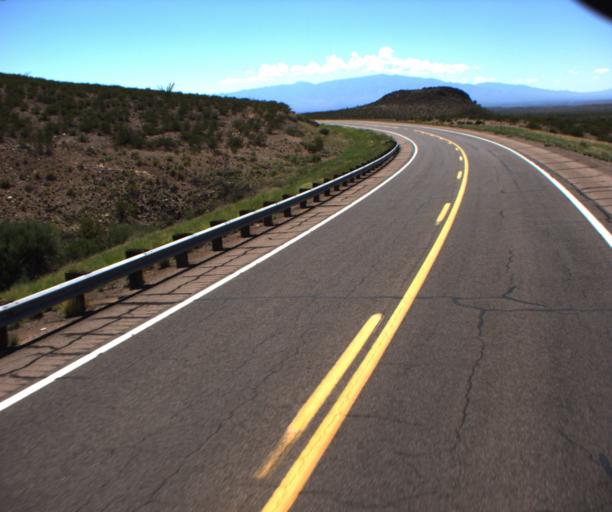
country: US
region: Arizona
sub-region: Greenlee County
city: Clifton
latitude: 32.8479
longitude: -109.4082
